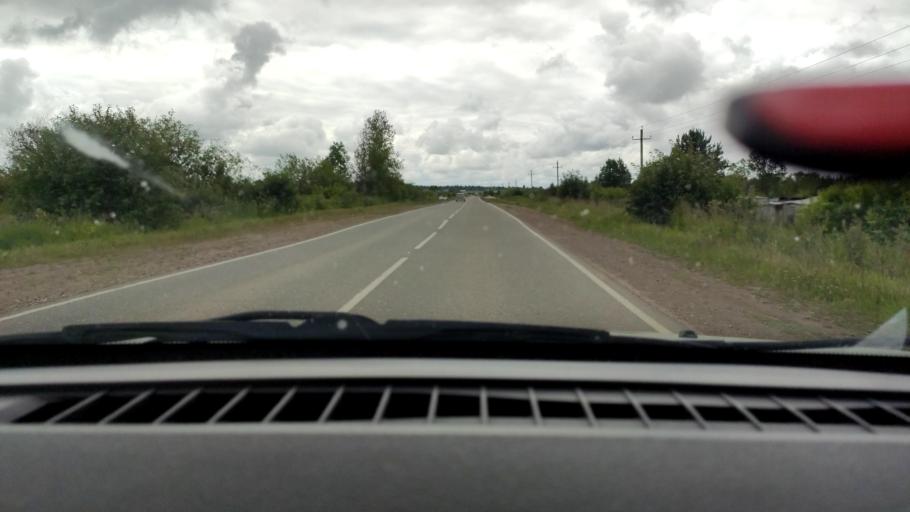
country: RU
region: Perm
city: Chaykovskaya
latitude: 58.0841
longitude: 55.6146
